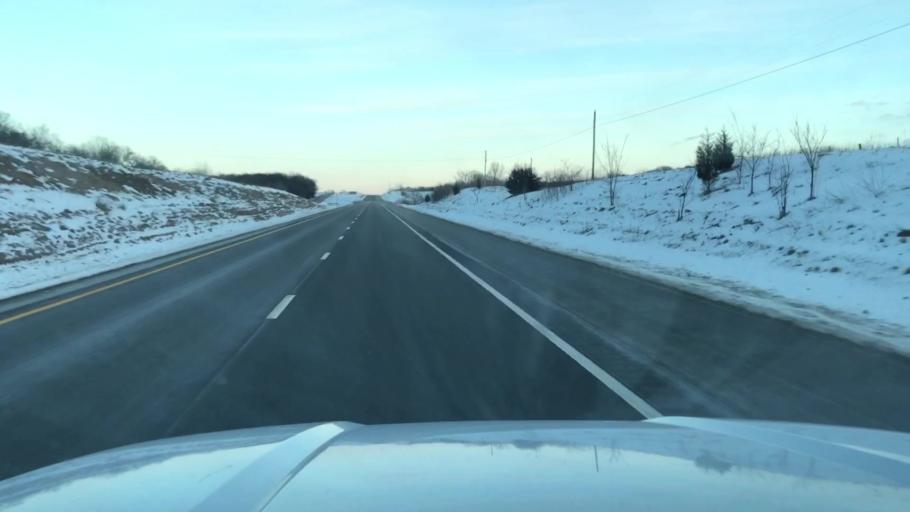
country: US
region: Missouri
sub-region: DeKalb County
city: Maysville
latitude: 39.7620
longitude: -94.4751
